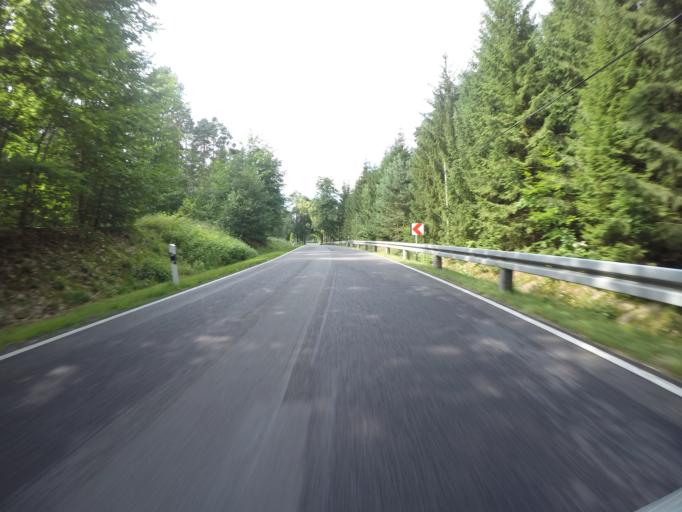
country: DE
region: Brandenburg
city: Rheinsberg
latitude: 53.1942
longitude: 12.8929
